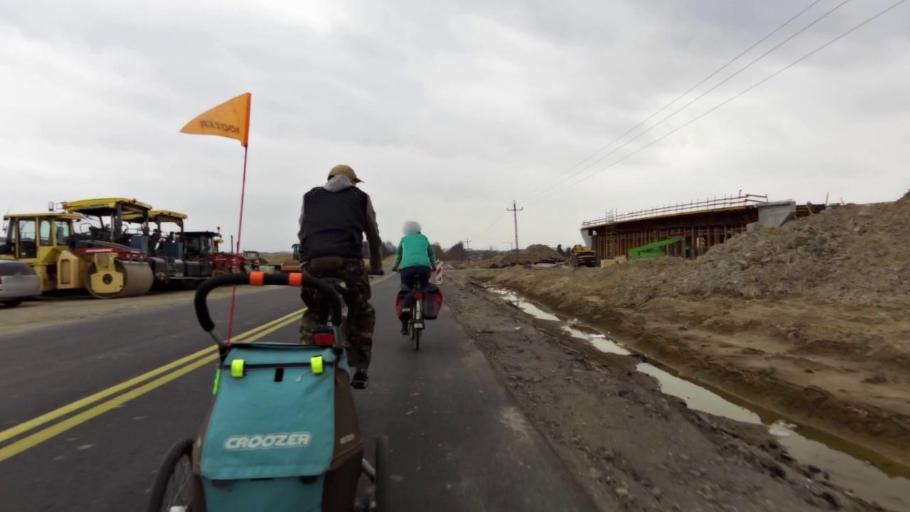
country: PL
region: West Pomeranian Voivodeship
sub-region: Koszalin
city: Koszalin
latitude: 54.2315
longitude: 16.1790
